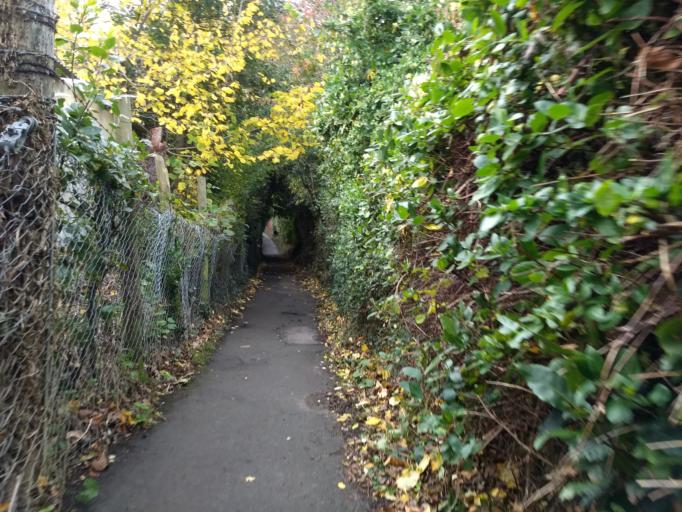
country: GB
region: England
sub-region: Isle of Wight
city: Totland
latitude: 50.6837
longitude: -1.5216
